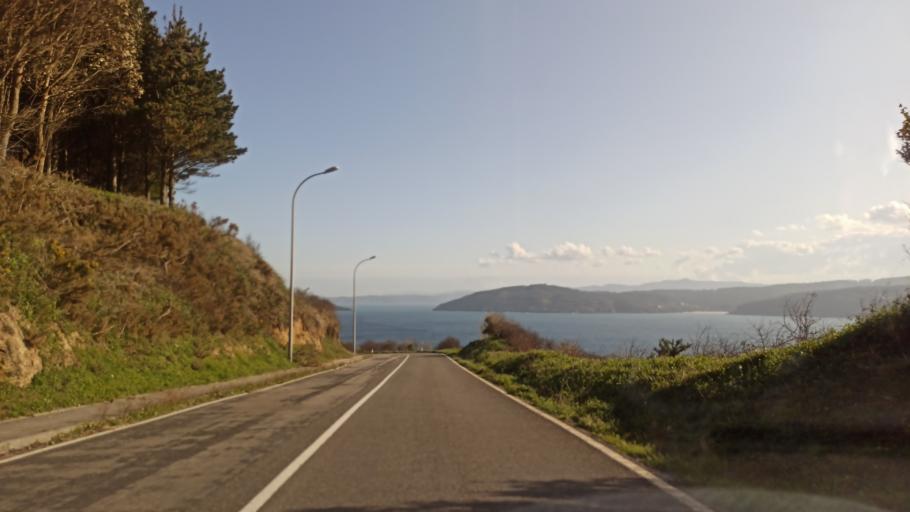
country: ES
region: Galicia
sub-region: Provincia da Coruna
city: Manon
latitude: 43.7725
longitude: -7.6803
